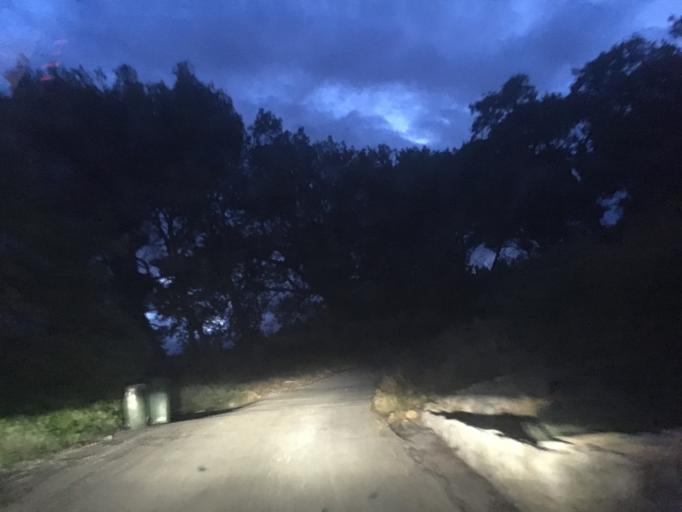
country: HR
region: Splitsko-Dalmatinska
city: Srinjine
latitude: 43.4631
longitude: 16.5962
